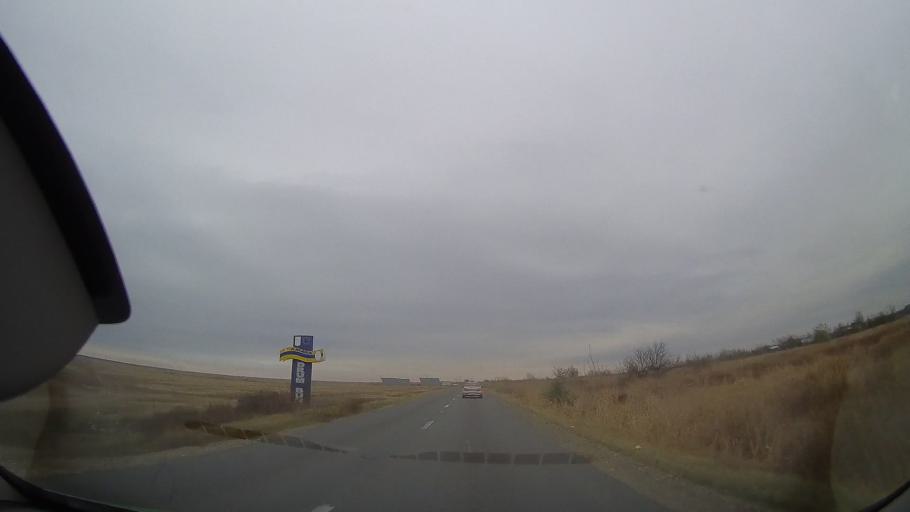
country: RO
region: Ialomita
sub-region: Oras Amara
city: Amara
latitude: 44.6231
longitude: 27.3014
